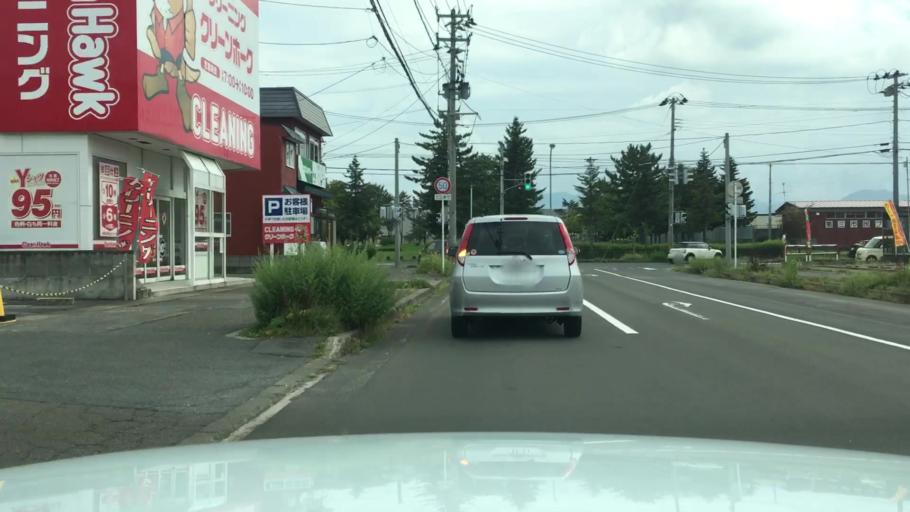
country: JP
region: Aomori
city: Hirosaki
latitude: 40.6179
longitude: 140.4843
